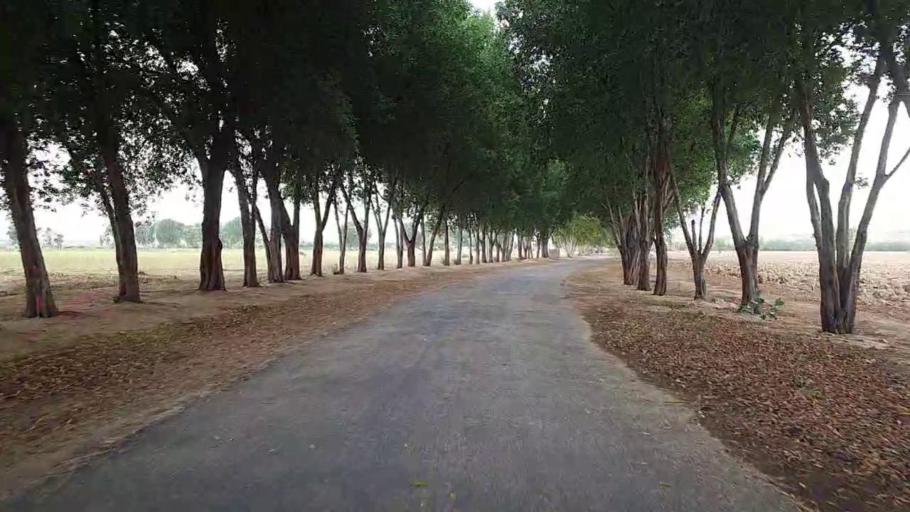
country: PK
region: Sindh
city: Jamshoro
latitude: 25.3959
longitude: 67.6990
